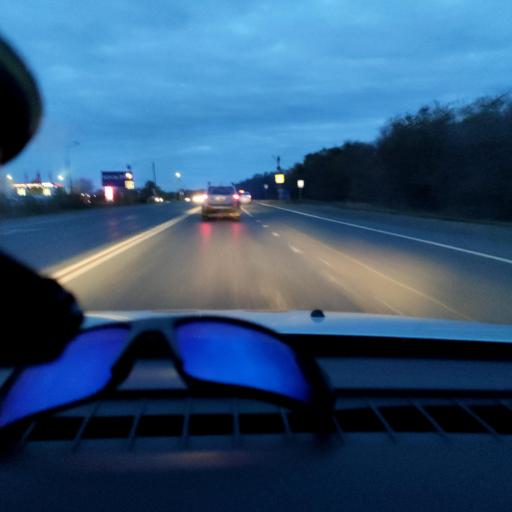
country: RU
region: Samara
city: Samara
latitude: 53.0811
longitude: 50.1211
